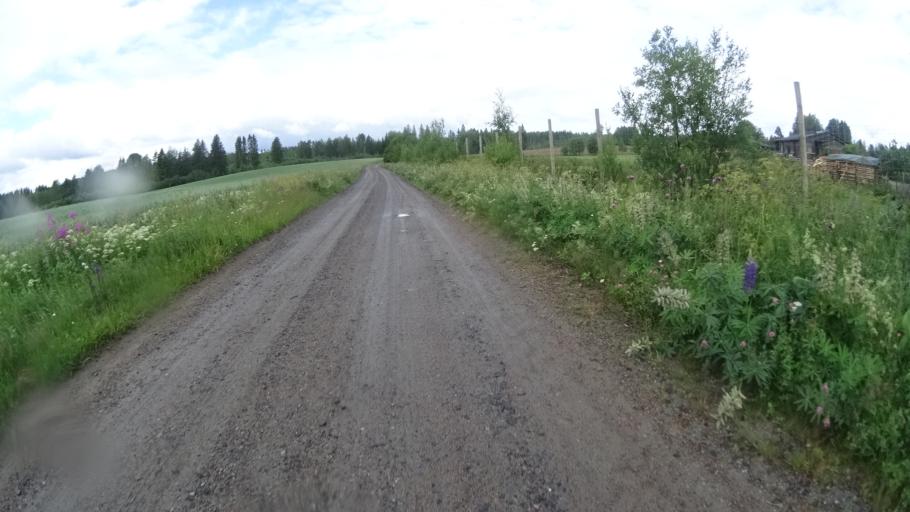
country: FI
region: Uusimaa
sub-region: Helsinki
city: Karkkila
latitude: 60.5849
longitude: 24.3410
